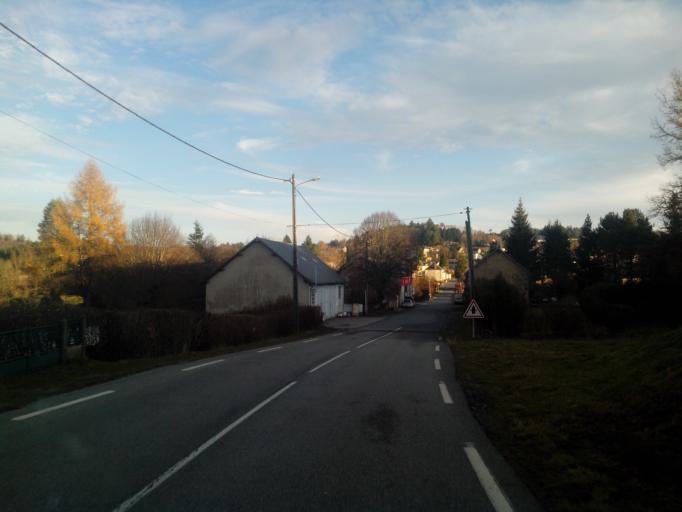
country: FR
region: Limousin
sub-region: Departement de la Correze
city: Bugeat
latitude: 45.6018
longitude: 1.9196
